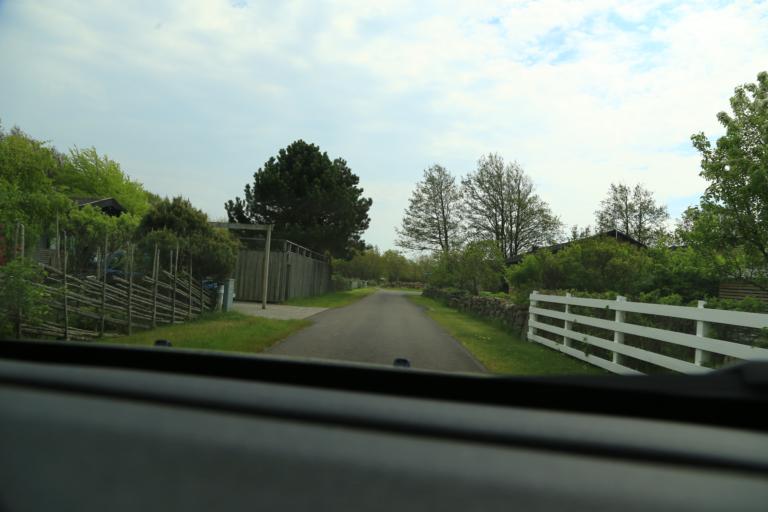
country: SE
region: Halland
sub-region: Varbergs Kommun
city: Varberg
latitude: 57.1482
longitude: 12.2139
